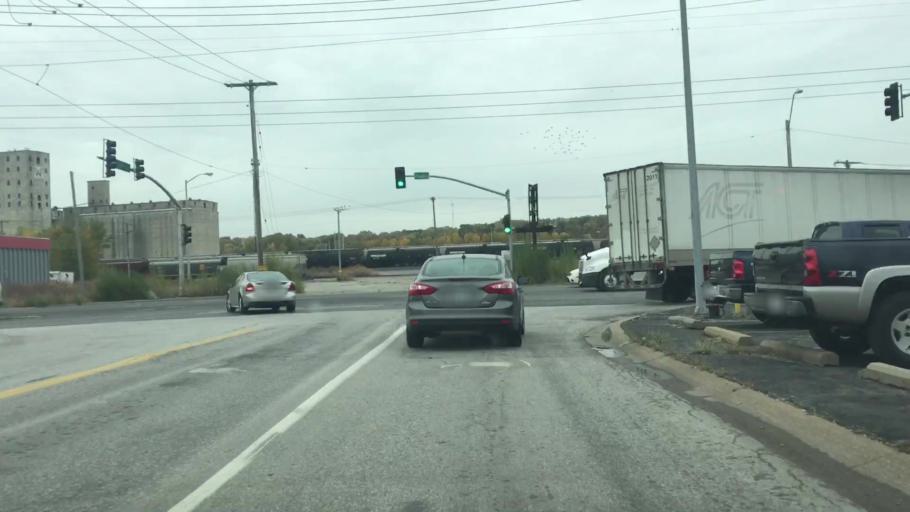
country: US
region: Missouri
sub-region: Clay County
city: North Kansas City
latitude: 39.1309
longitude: -94.5143
